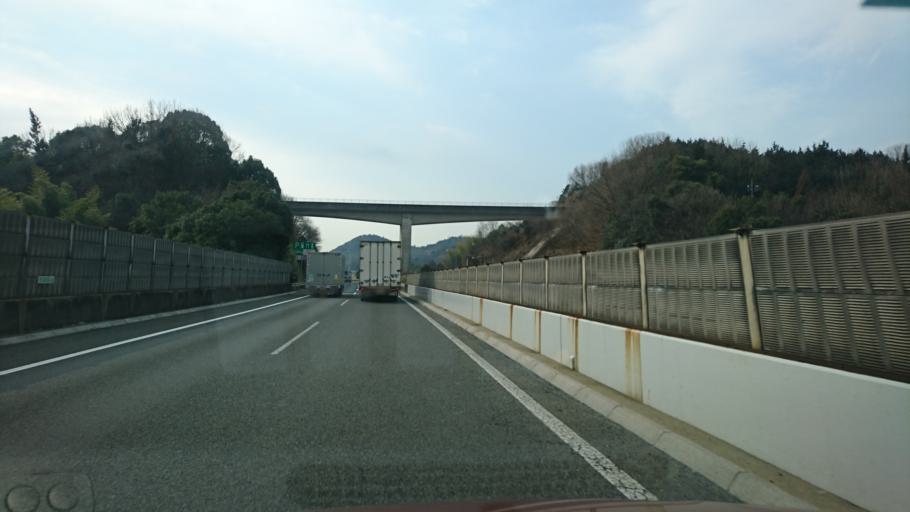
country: JP
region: Hiroshima
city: Fukuyama
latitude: 34.4956
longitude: 133.3180
